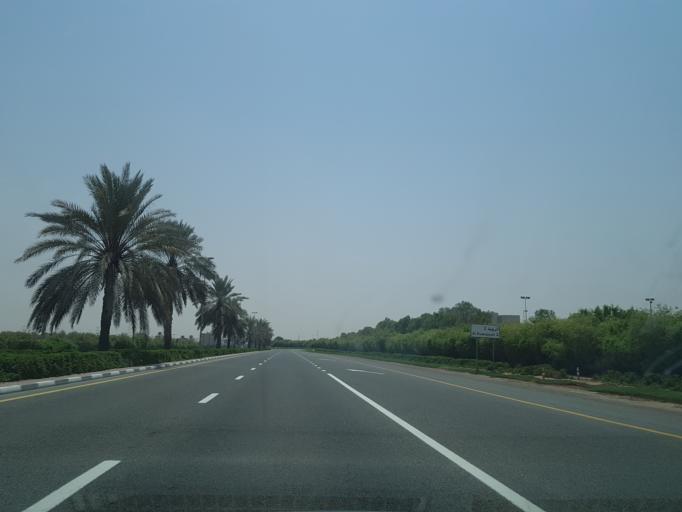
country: AE
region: Ash Shariqah
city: Sharjah
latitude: 25.1124
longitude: 55.3941
